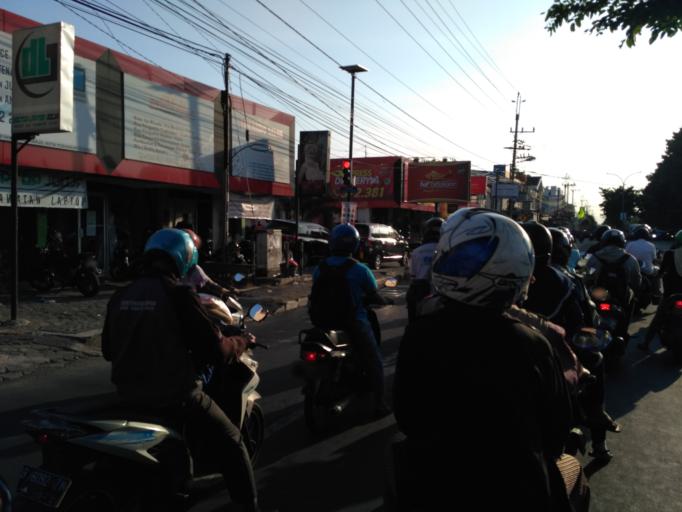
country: ID
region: Daerah Istimewa Yogyakarta
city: Yogyakarta
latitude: -7.8170
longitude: 110.3843
